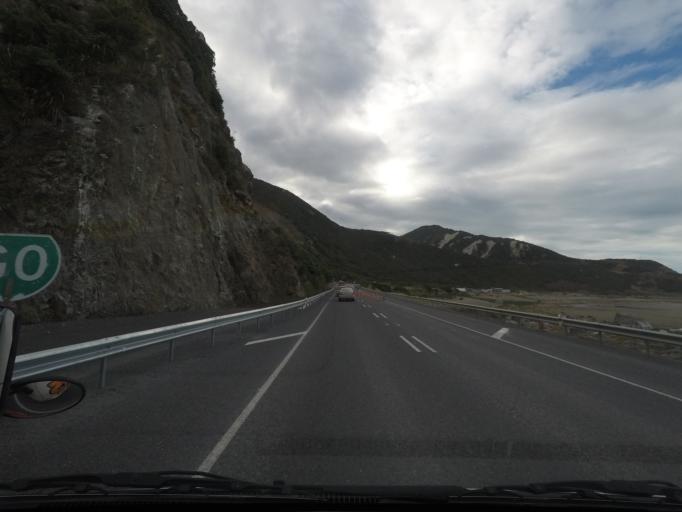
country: NZ
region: Canterbury
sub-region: Kaikoura District
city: Kaikoura
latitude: -42.2207
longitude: 173.8569
